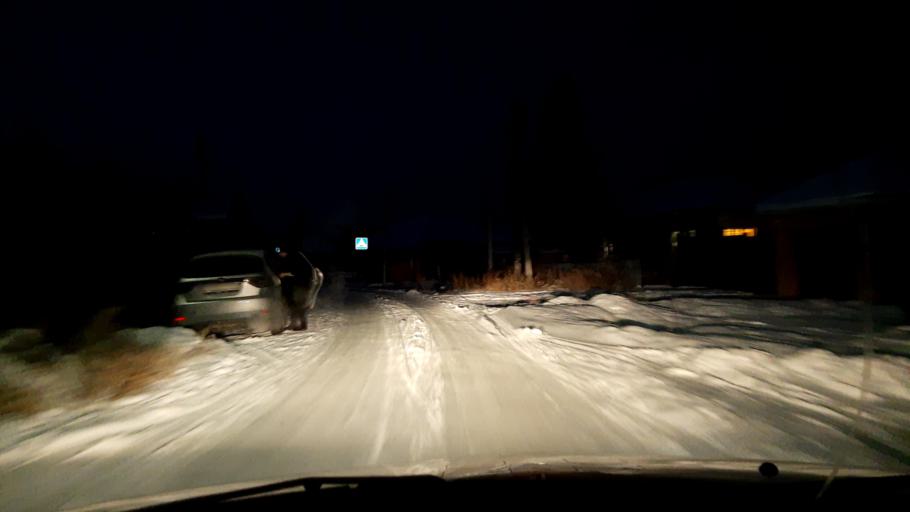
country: RU
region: Bashkortostan
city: Ufa
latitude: 54.6131
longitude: 55.9512
